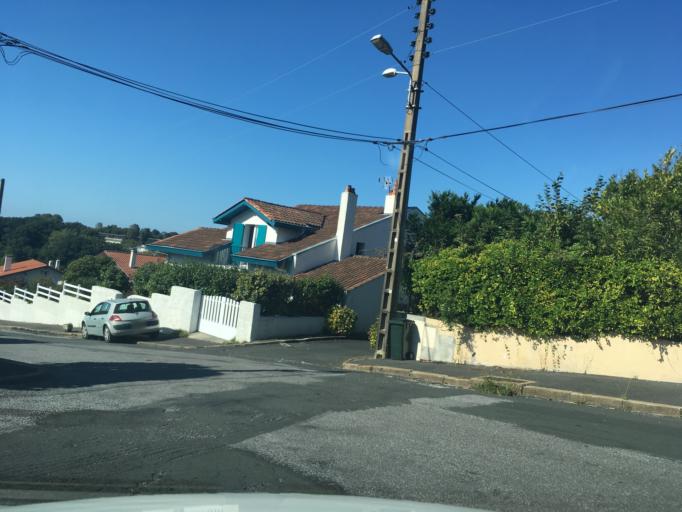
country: FR
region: Aquitaine
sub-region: Departement des Pyrenees-Atlantiques
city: Arbonne
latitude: 43.4566
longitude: -1.5485
